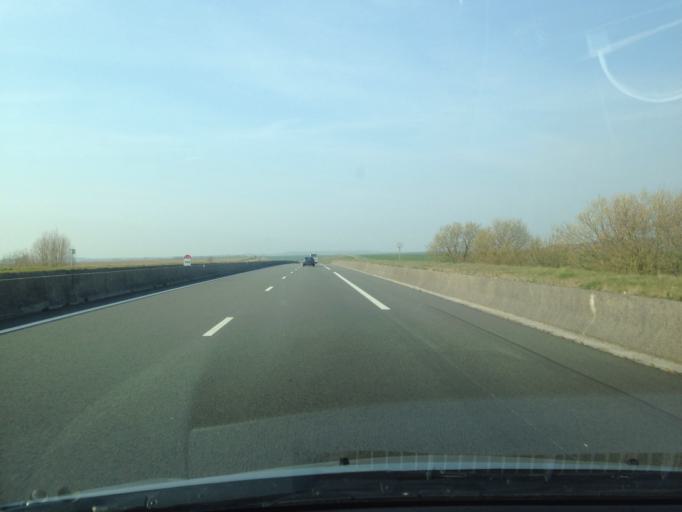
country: FR
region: Picardie
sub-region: Departement de la Somme
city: Rue
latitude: 50.3143
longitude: 1.7223
